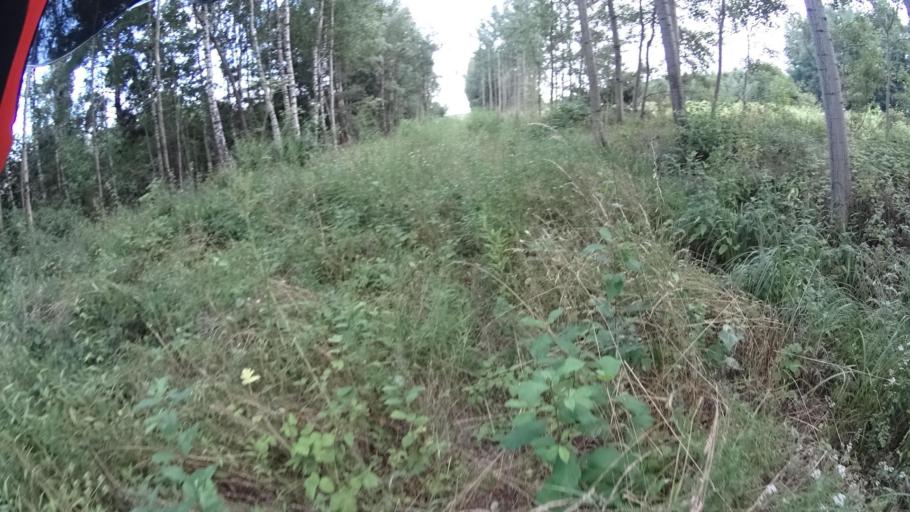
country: PL
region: Masovian Voivodeship
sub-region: Powiat piaseczynski
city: Tarczyn
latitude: 51.9678
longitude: 20.8688
